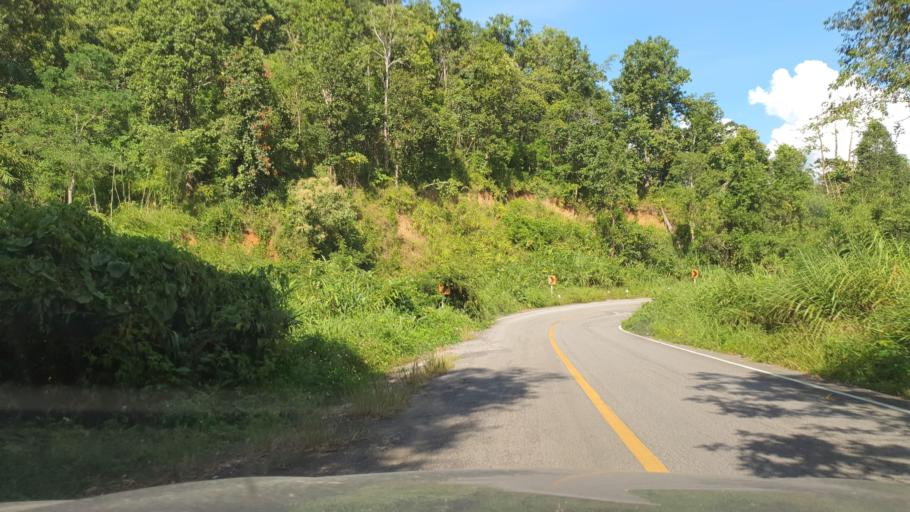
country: TH
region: Chiang Rai
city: Wiang Pa Pao
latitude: 19.3316
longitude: 99.4522
